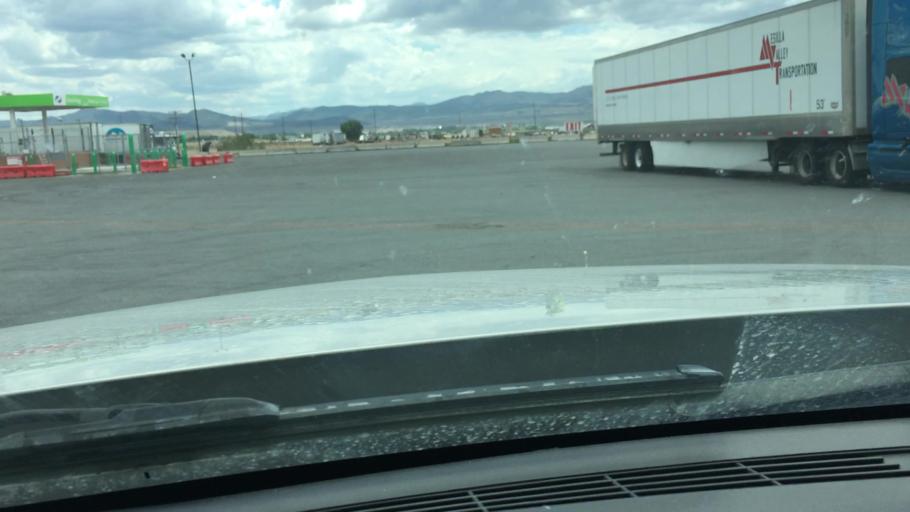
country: US
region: Utah
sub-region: Beaver County
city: Beaver
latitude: 38.2927
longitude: -112.6537
